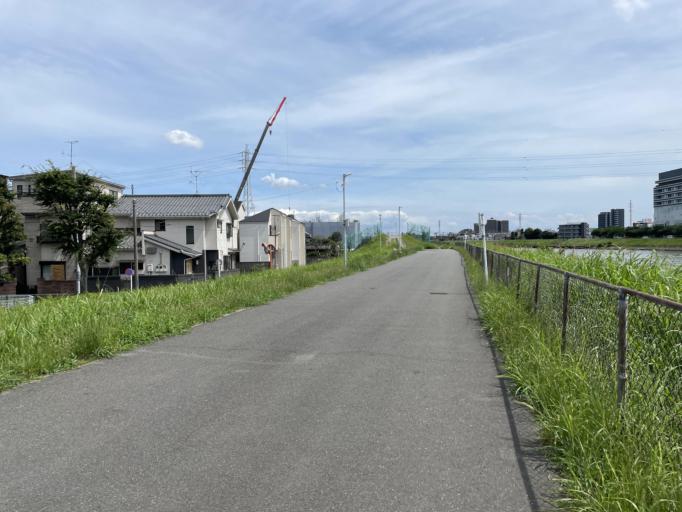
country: JP
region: Chiba
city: Matsudo
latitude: 35.7550
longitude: 139.8596
